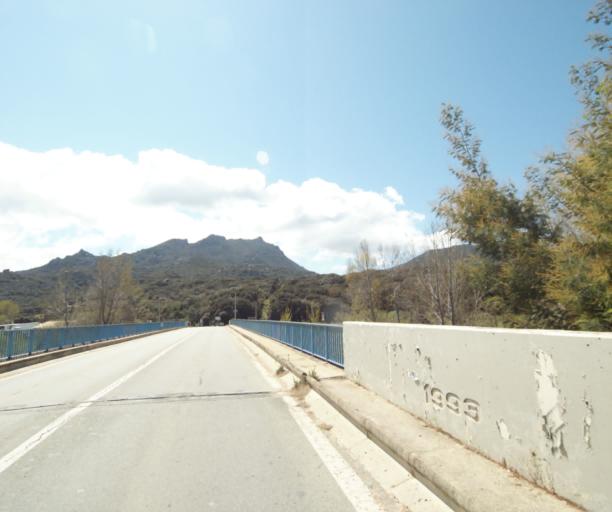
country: FR
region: Corsica
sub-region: Departement de la Corse-du-Sud
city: Propriano
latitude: 41.6579
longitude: 8.9176
